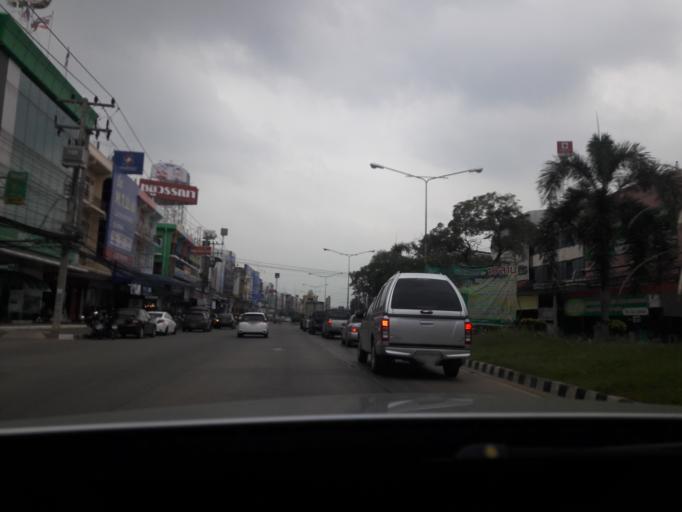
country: TH
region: Samut Songkhram
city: Samut Songkhram
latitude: 13.4029
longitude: 100.0034
